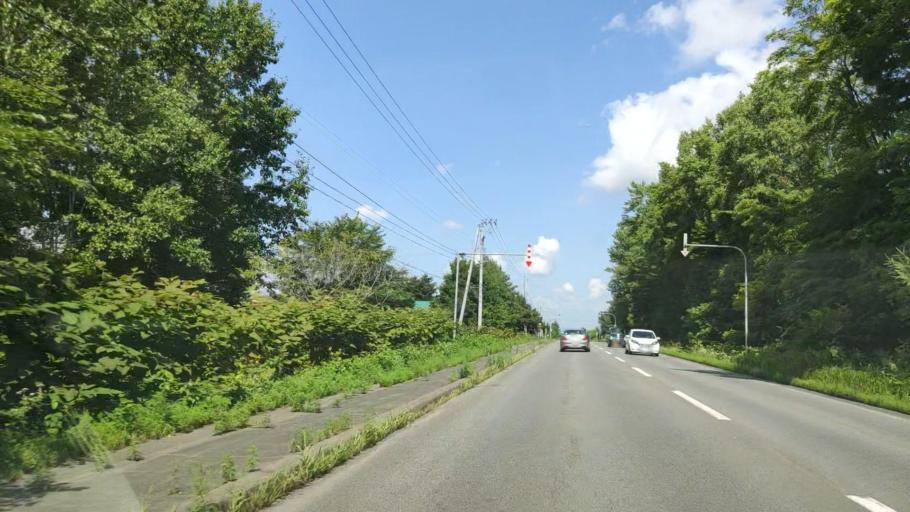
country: JP
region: Hokkaido
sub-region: Asahikawa-shi
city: Asahikawa
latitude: 43.6341
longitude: 142.4572
